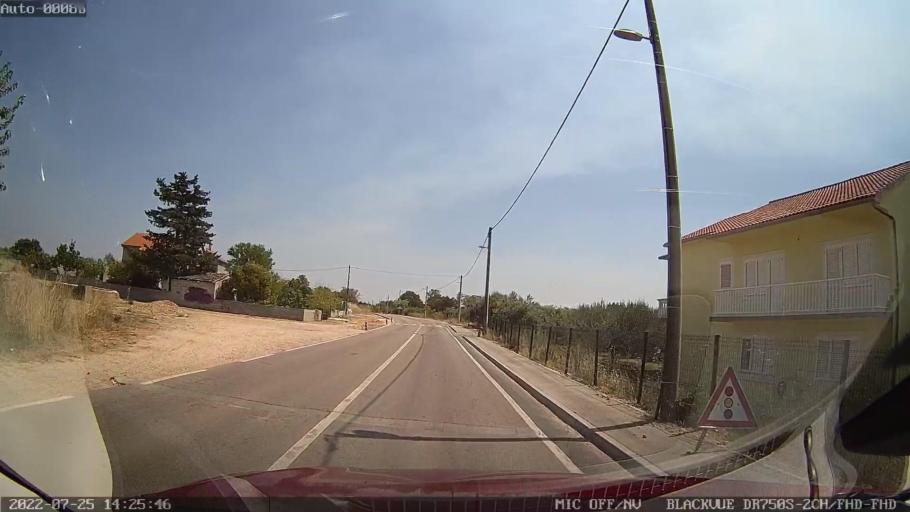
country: HR
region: Zadarska
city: Policnik
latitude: 44.1427
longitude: 15.3337
